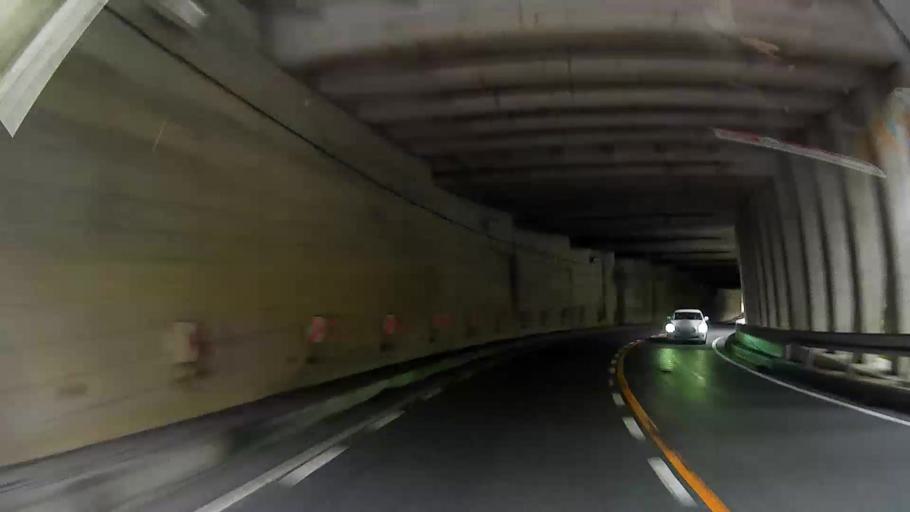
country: JP
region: Yamanashi
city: Enzan
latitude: 35.9134
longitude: 138.8209
